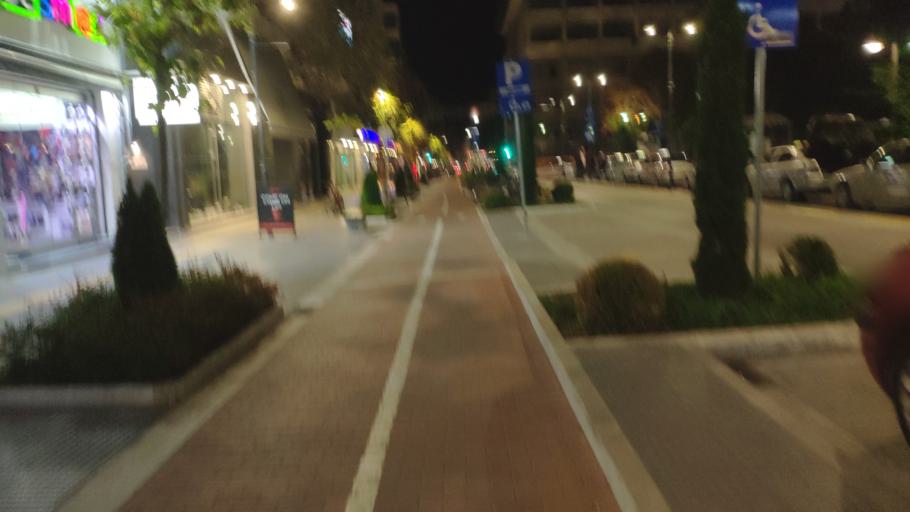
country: GR
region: Thessaly
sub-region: Nomos Larisis
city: Larisa
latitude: 39.6384
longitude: 22.4168
